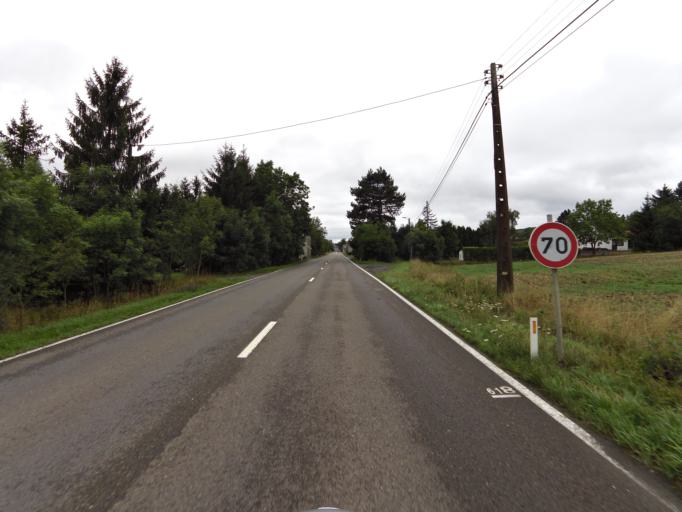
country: BE
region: Wallonia
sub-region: Province du Luxembourg
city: Wellin
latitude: 50.1098
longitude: 5.1530
